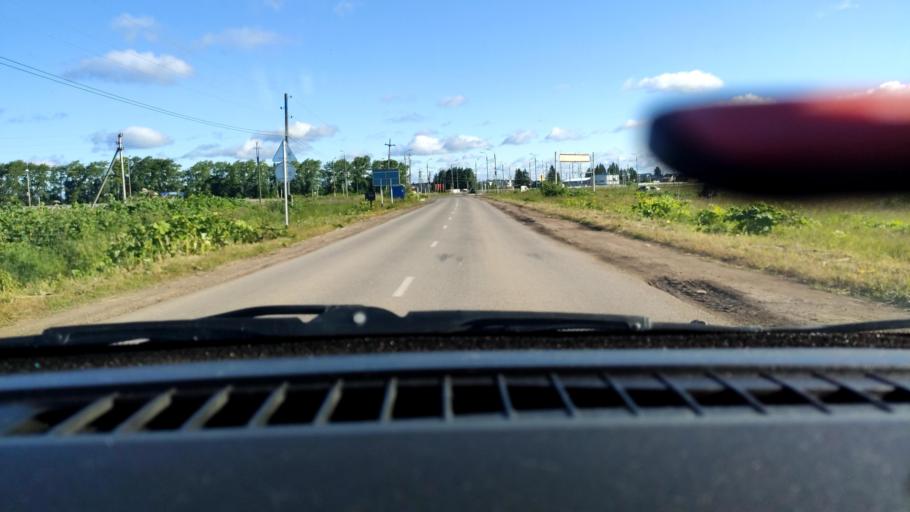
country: RU
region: Perm
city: Kultayevo
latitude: 57.8830
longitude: 55.9232
